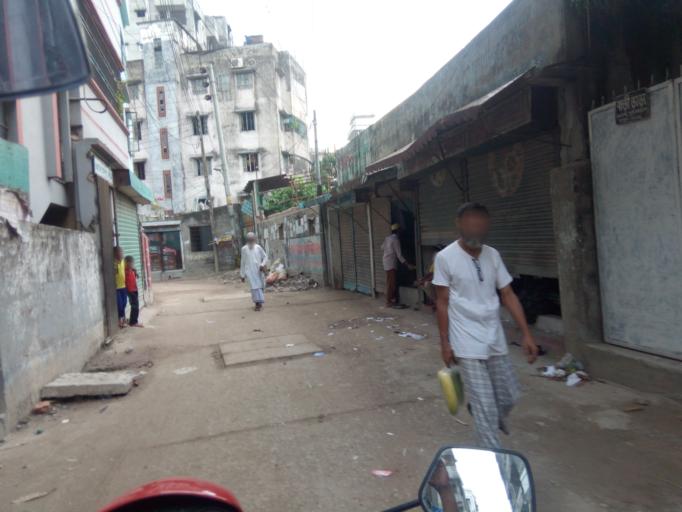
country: BD
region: Dhaka
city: Paltan
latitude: 23.7479
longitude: 90.4383
